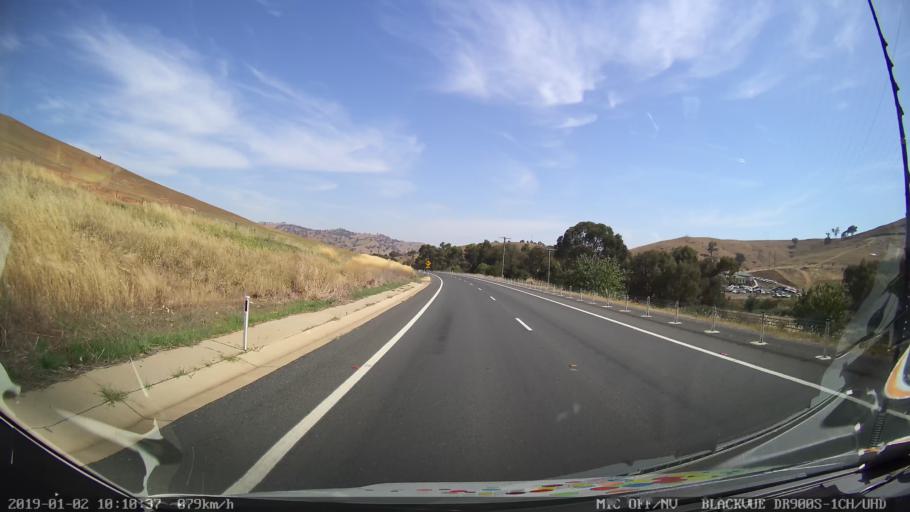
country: AU
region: New South Wales
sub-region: Gundagai
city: Gundagai
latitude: -35.1016
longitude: 148.0960
